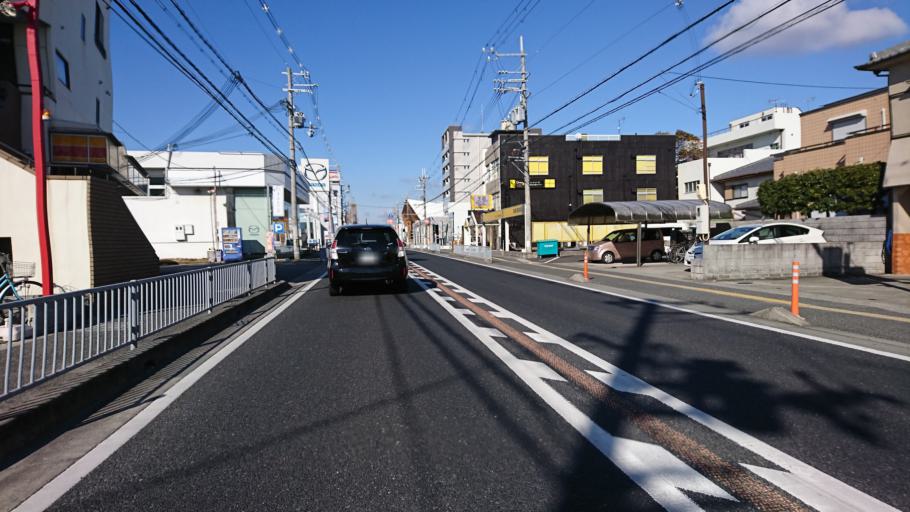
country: JP
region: Hyogo
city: Kakogawacho-honmachi
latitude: 34.7415
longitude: 134.8693
